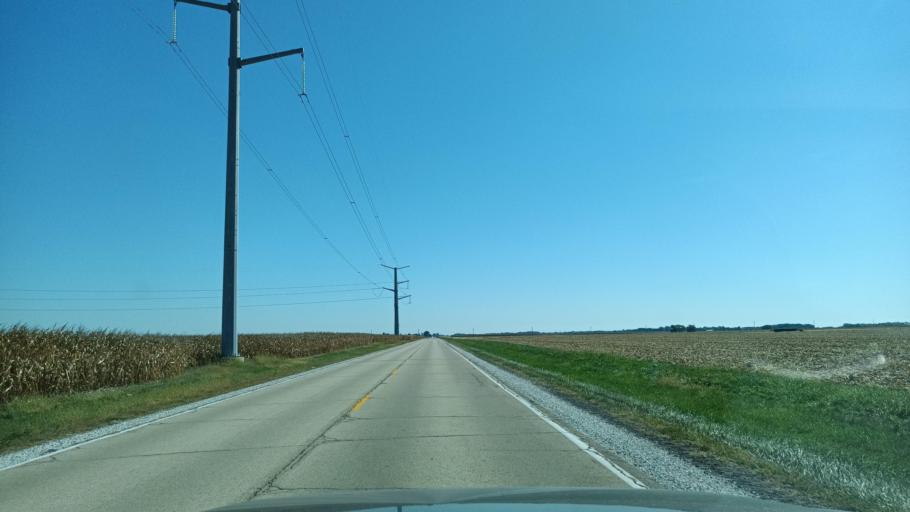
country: US
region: Illinois
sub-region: Peoria County
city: Elmwood
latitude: 40.9022
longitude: -89.9788
